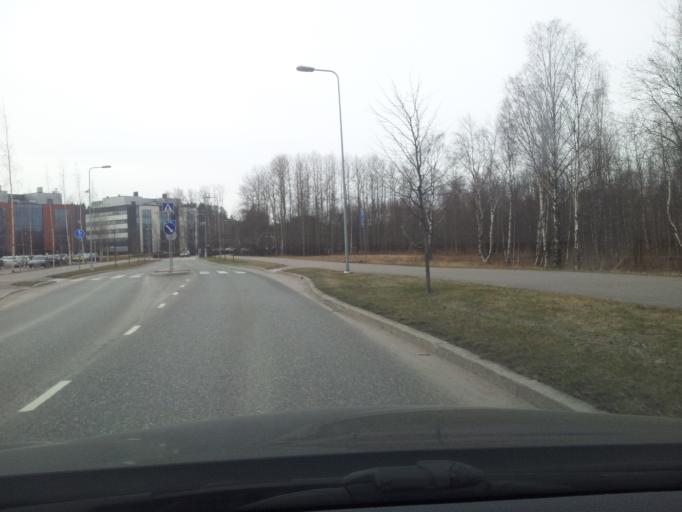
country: FI
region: Uusimaa
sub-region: Helsinki
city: Teekkarikylae
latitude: 60.2113
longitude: 24.8293
